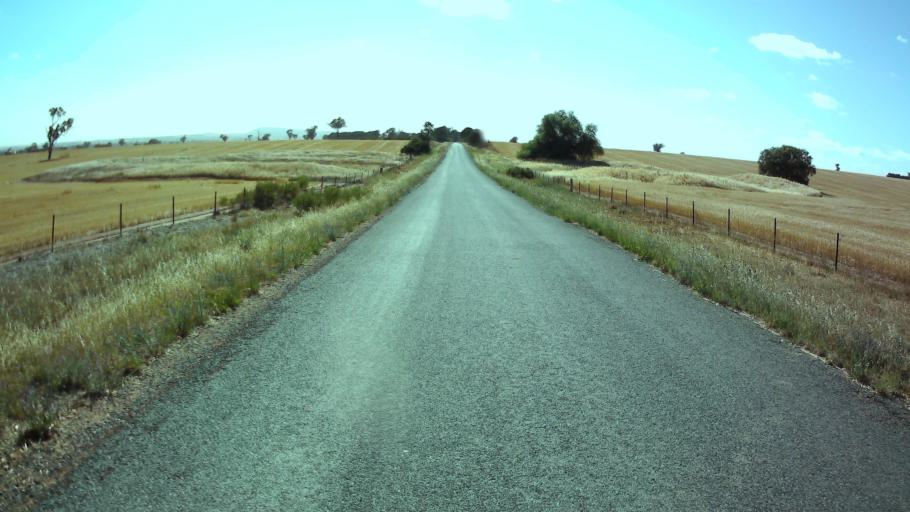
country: AU
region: New South Wales
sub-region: Weddin
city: Grenfell
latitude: -34.0613
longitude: 148.2527
